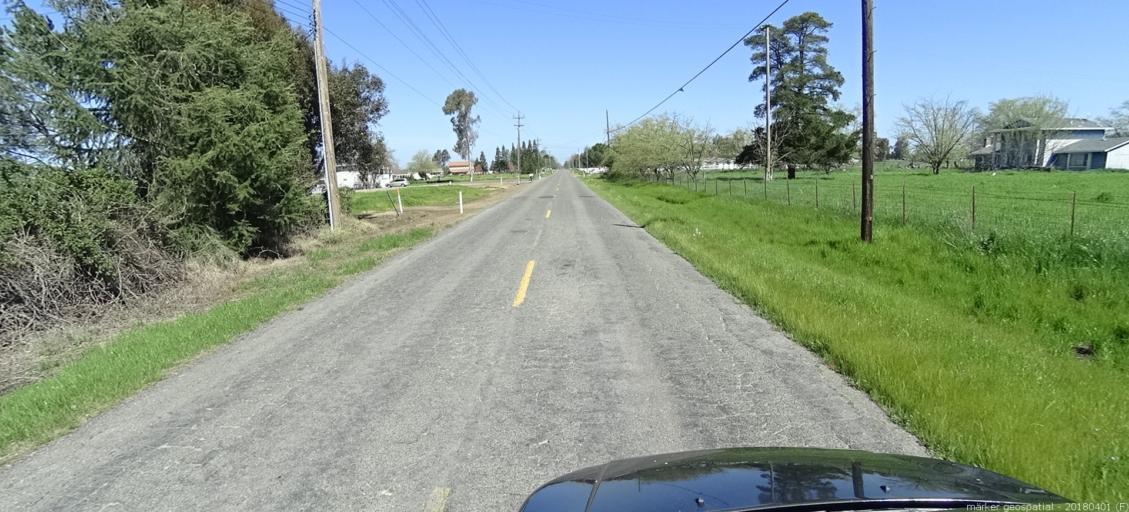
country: US
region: California
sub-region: Sacramento County
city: Herald
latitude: 38.3309
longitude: -121.2421
